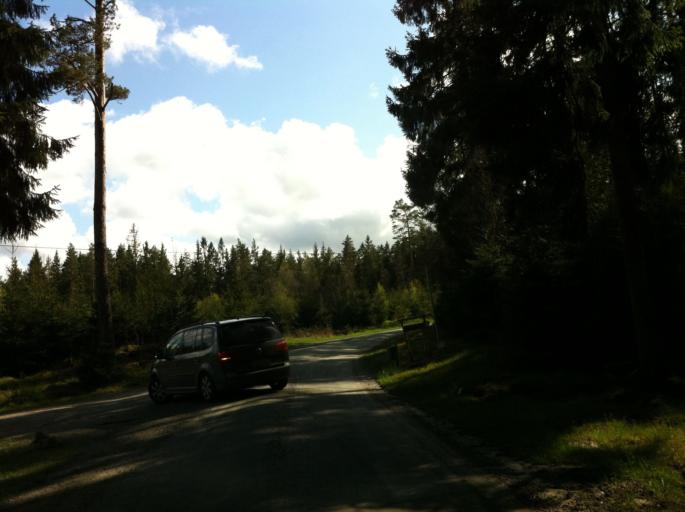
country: SE
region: Vaestra Goetaland
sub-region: Bollebygds Kommun
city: Bollebygd
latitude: 57.7742
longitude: 12.5982
